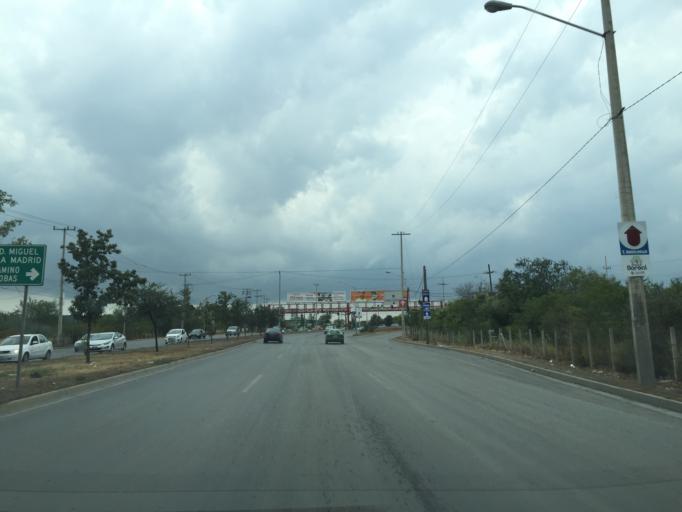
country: MX
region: Nuevo Leon
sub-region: Juarez
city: Valle de Juarez
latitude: 25.6791
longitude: -100.1685
